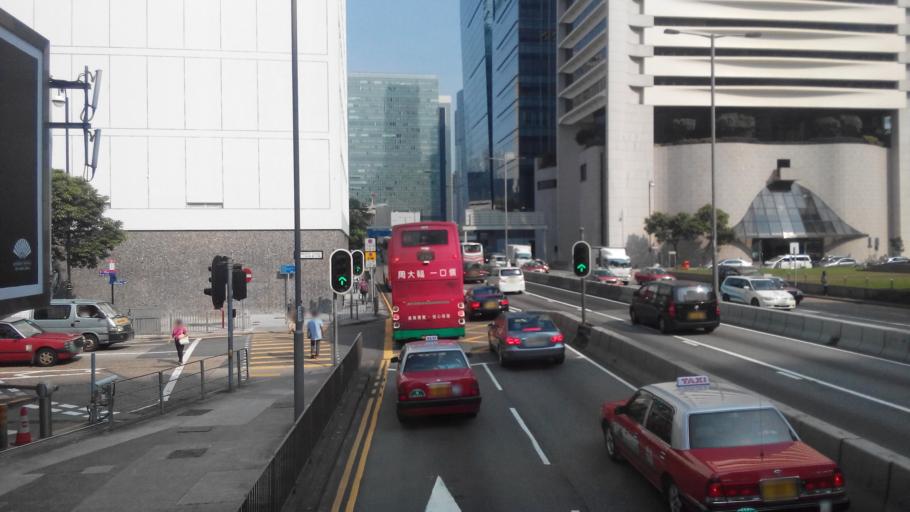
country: HK
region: Central and Western
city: Central
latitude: 22.2825
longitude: 114.1604
